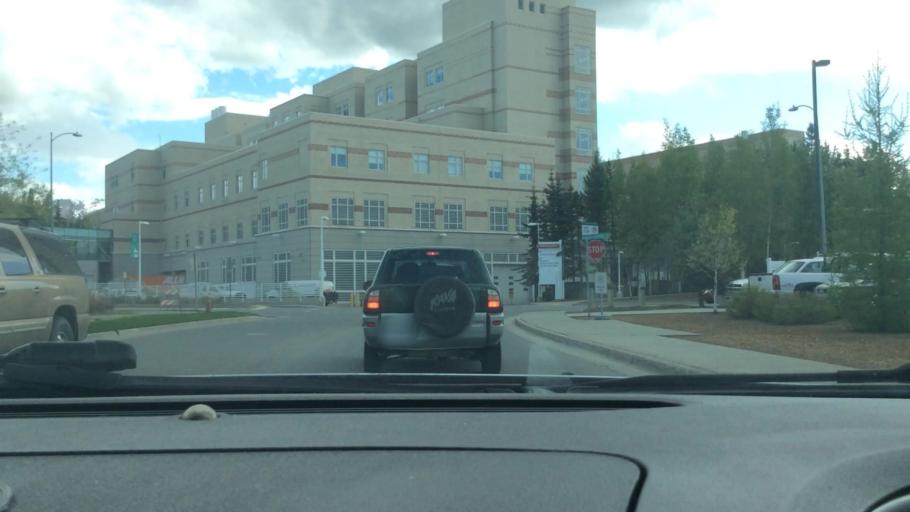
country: US
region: Alaska
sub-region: Anchorage Municipality
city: Anchorage
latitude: 61.1833
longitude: -149.8030
